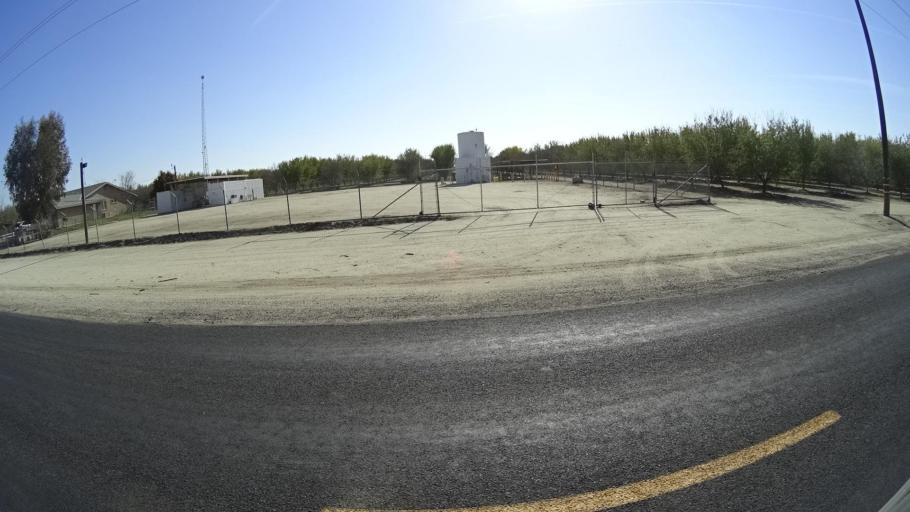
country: US
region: California
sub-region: Kern County
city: McFarland
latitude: 35.6453
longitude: -119.2699
